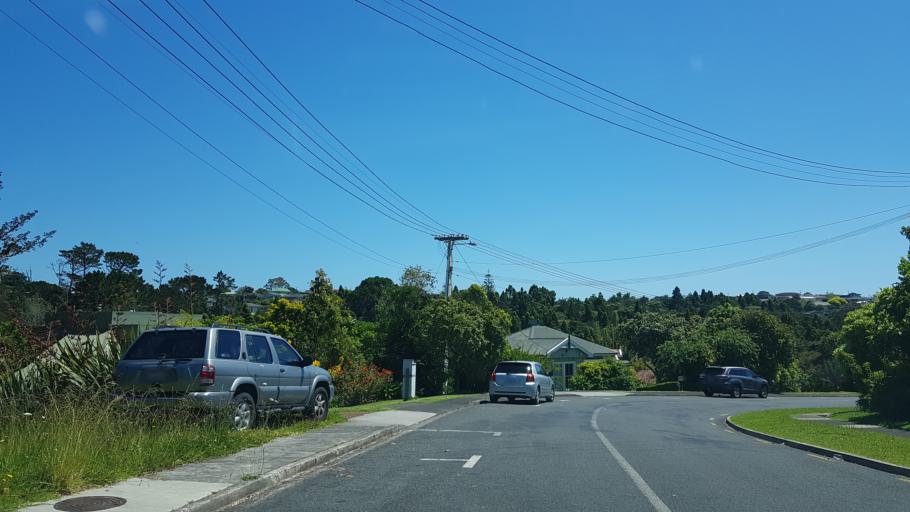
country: NZ
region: Auckland
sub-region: Auckland
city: North Shore
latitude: -36.8081
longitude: 174.7321
